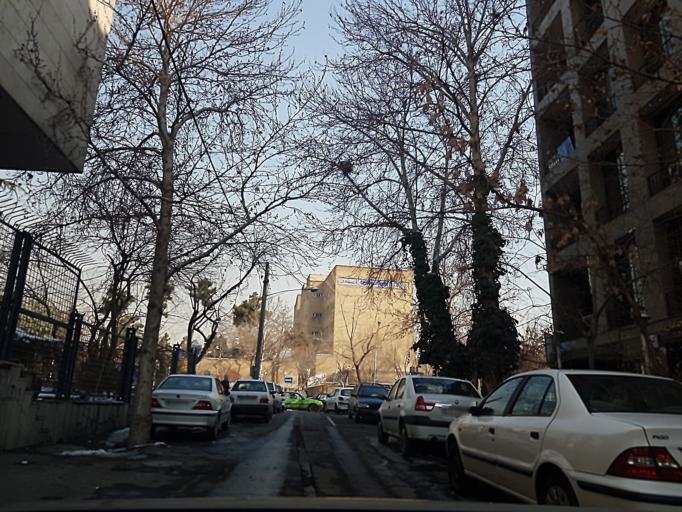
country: IR
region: Tehran
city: Tehran
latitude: 35.7257
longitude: 51.4271
